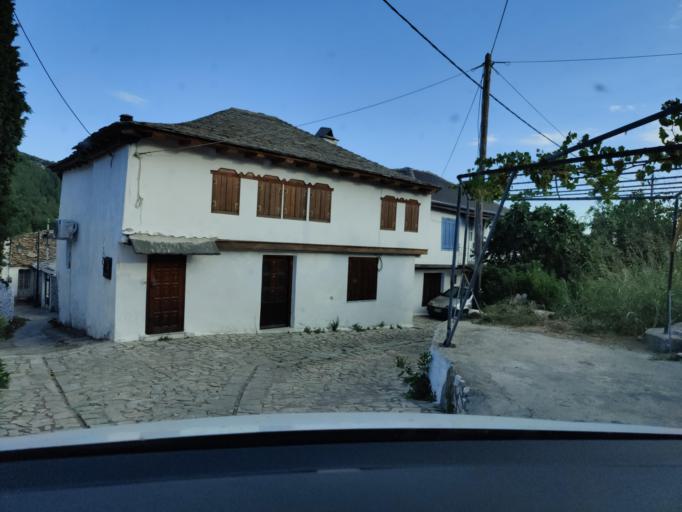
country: GR
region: East Macedonia and Thrace
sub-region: Nomos Kavalas
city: Potamia
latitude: 40.6584
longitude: 24.6914
